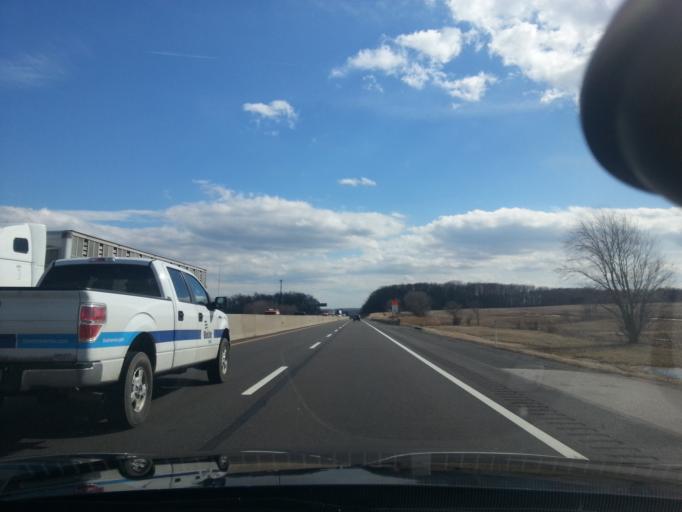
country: US
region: Pennsylvania
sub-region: Montgomery County
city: Harleysville
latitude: 40.2862
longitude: -75.3638
